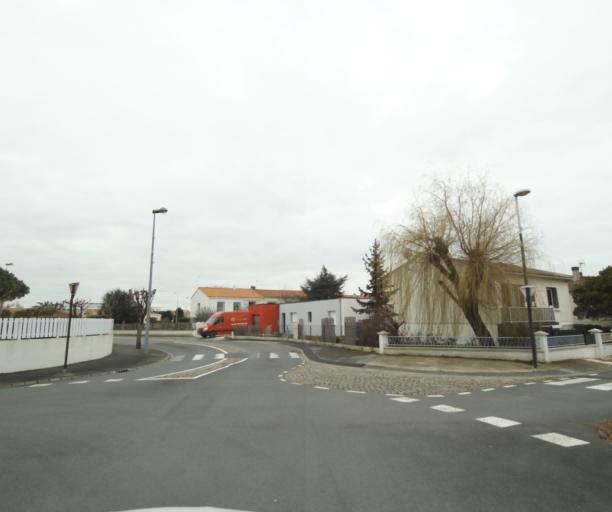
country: FR
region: Poitou-Charentes
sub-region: Departement de la Charente-Maritime
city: Lagord
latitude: 46.1867
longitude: -1.1552
